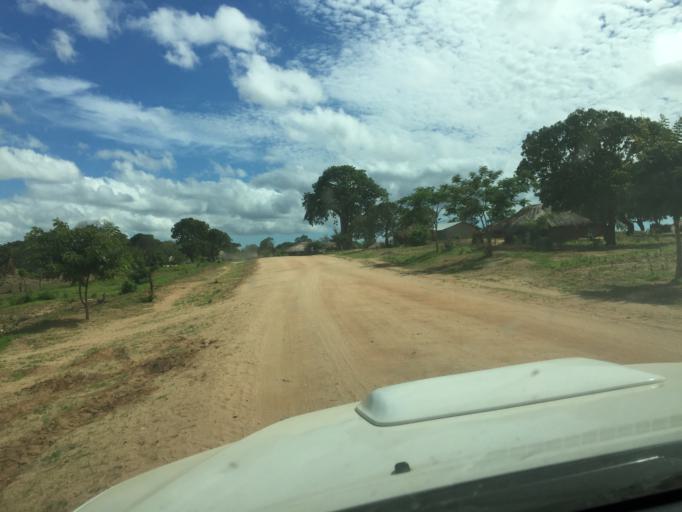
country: MZ
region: Nampula
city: Nacala
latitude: -14.2375
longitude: 40.5084
